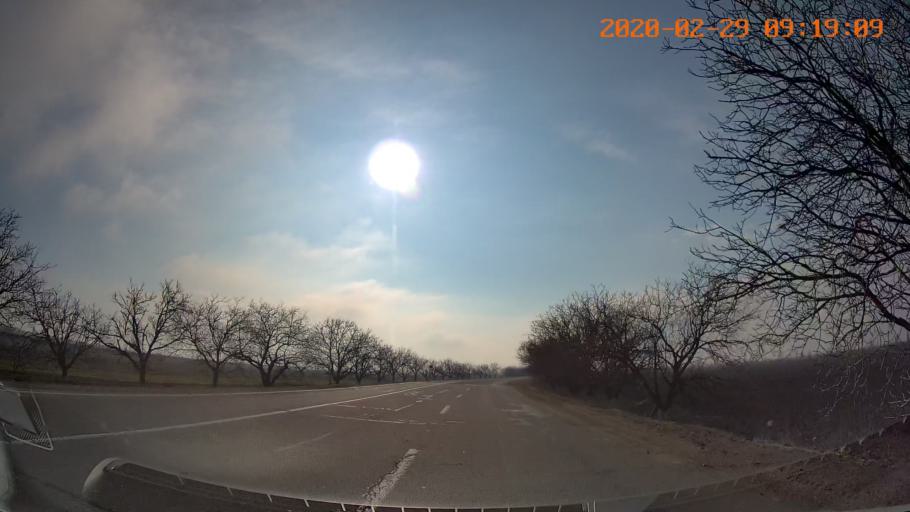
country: MD
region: Telenesti
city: Pervomaisc
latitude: 46.7666
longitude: 29.9360
